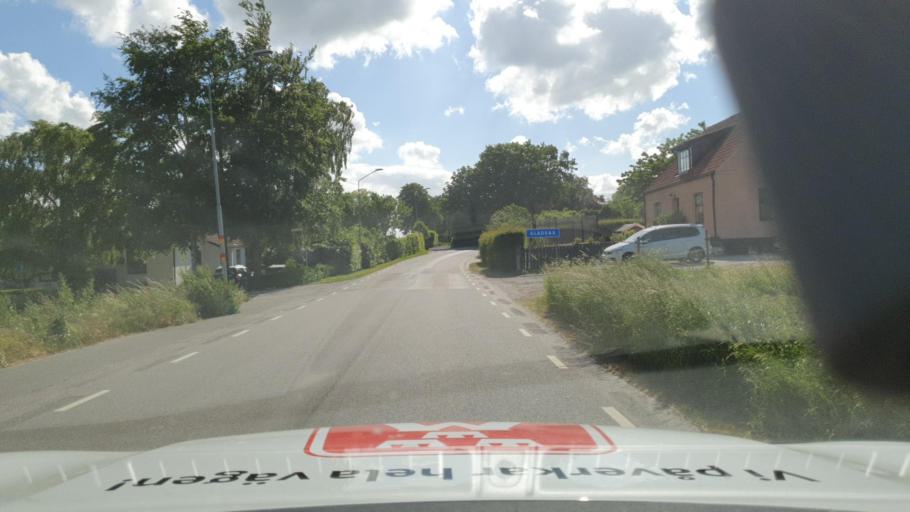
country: SE
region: Skane
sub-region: Simrishamns Kommun
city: Simrishamn
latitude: 55.5621
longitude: 14.2921
